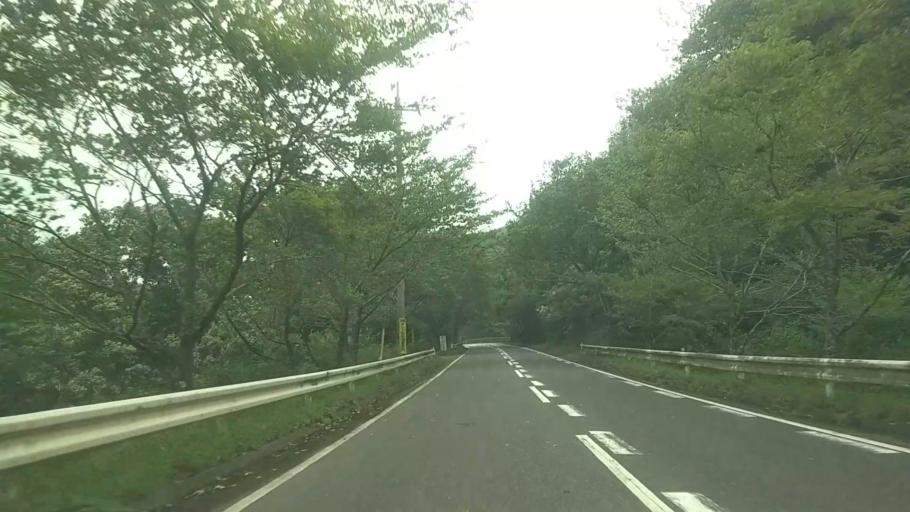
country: JP
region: Chiba
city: Kimitsu
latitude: 35.2301
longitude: 139.9643
